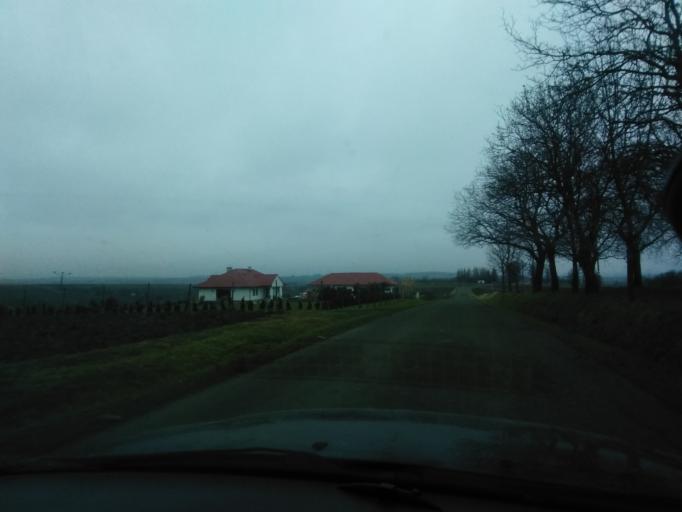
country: PL
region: Subcarpathian Voivodeship
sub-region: Powiat jaroslawski
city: Pruchnik
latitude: 49.9153
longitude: 22.5345
